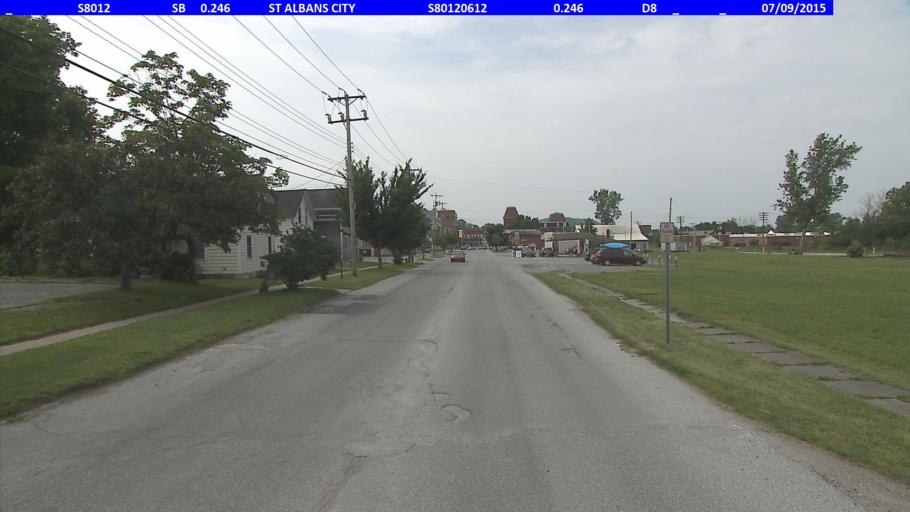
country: US
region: Vermont
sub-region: Franklin County
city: Saint Albans
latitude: 44.8144
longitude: -73.0851
